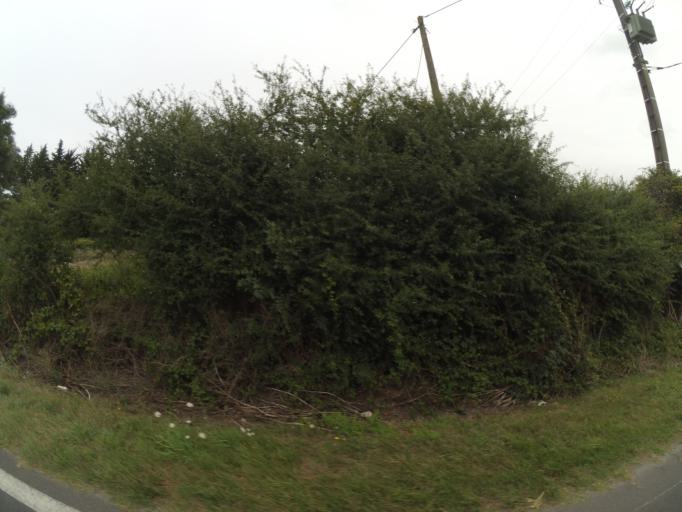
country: FR
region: Pays de la Loire
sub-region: Departement de la Vendee
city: Sallertaine
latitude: 46.8624
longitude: -1.9158
